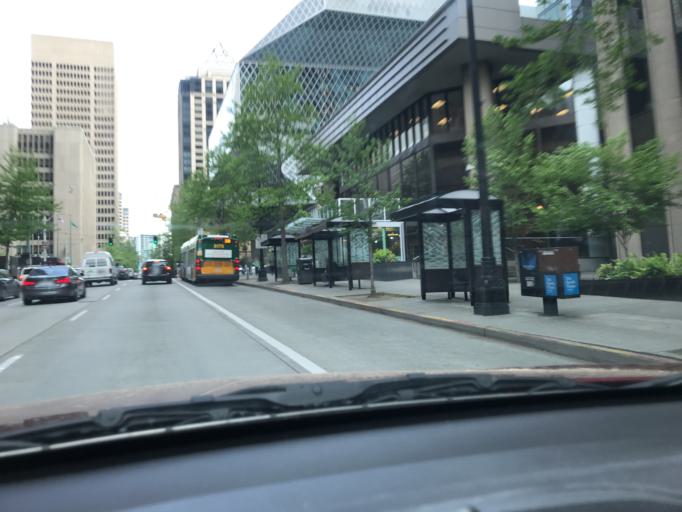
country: US
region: Washington
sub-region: King County
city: Seattle
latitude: 47.6054
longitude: -122.3323
